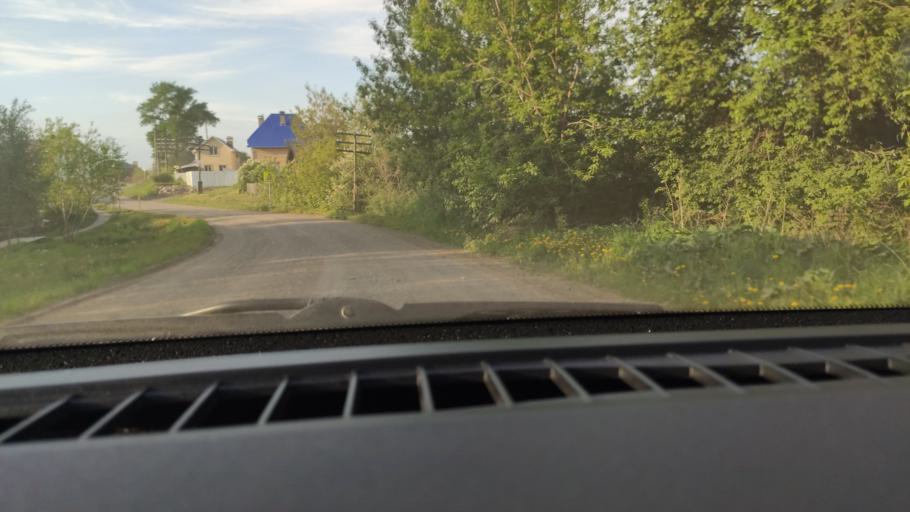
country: RU
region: Perm
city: Kultayevo
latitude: 57.9301
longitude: 56.0163
